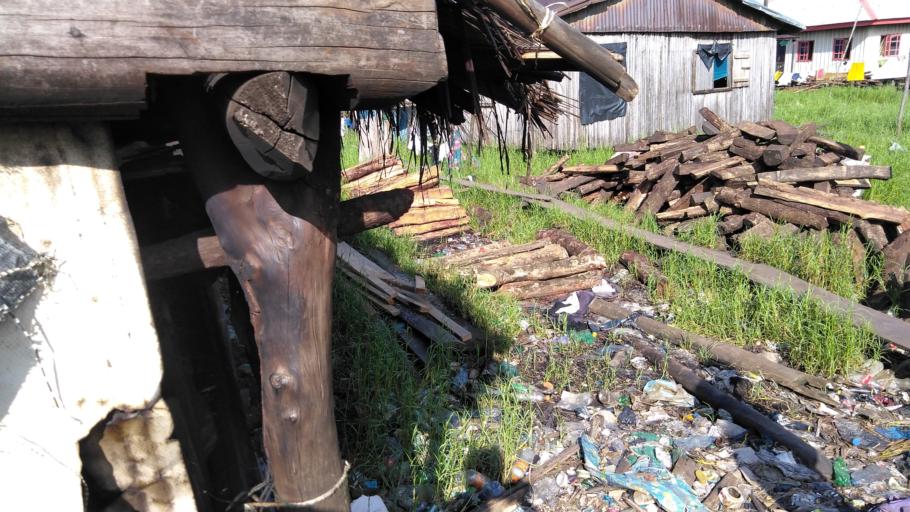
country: NG
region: Ondo
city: Igbekebo
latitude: 5.9206
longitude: 4.9692
